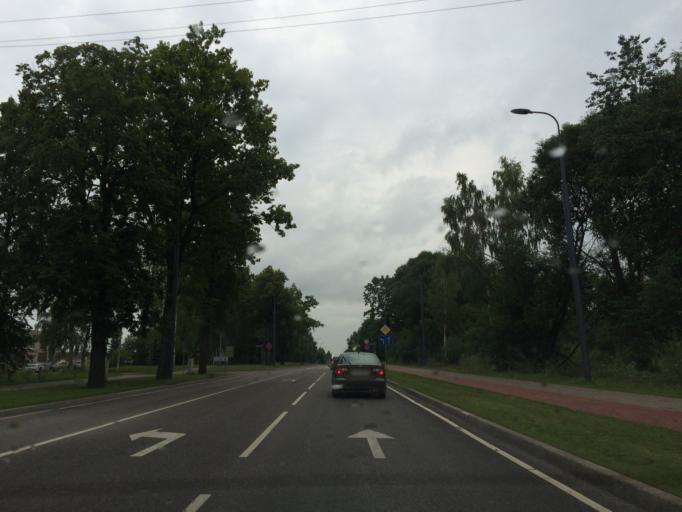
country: LV
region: Rezekne
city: Rezekne
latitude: 56.5331
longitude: 27.3470
